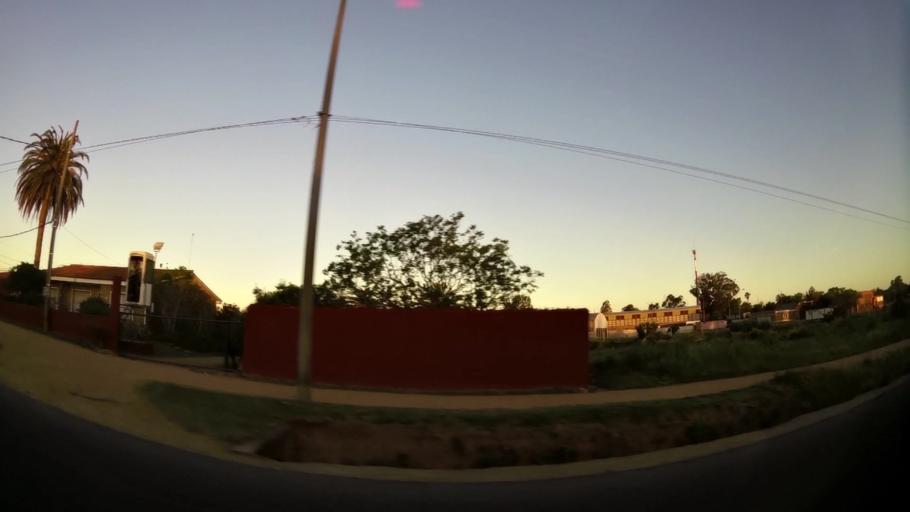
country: UY
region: Canelones
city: La Paz
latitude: -34.8219
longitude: -56.1690
